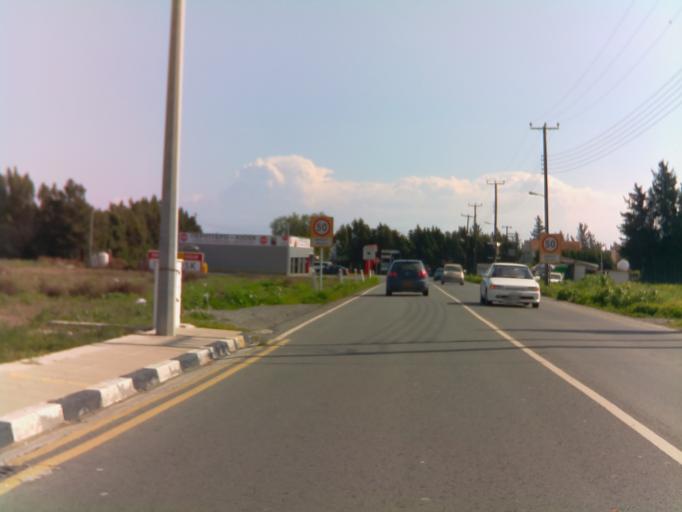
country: CY
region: Larnaka
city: Meneou
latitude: 34.8678
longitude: 33.5977
